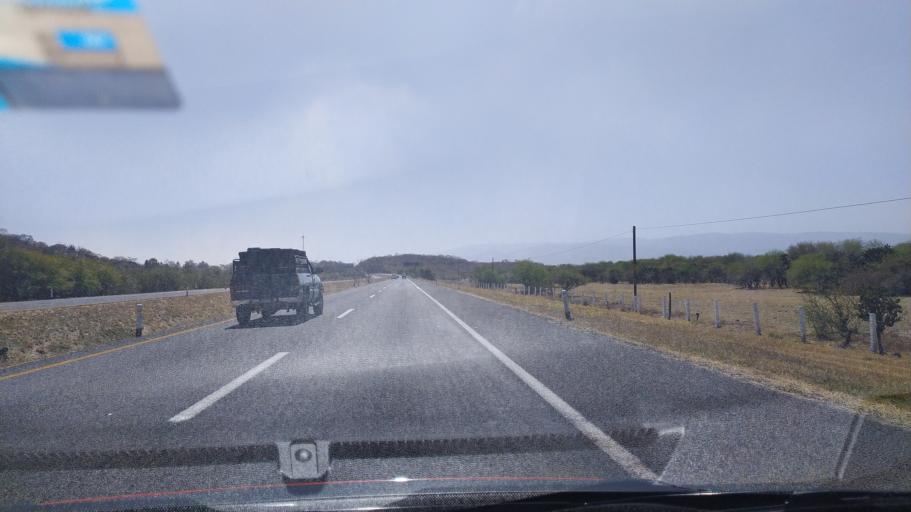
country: MX
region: Jalisco
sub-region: Acatlan de Juarez
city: Villa de los Ninos
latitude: 20.3597
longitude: -103.5764
